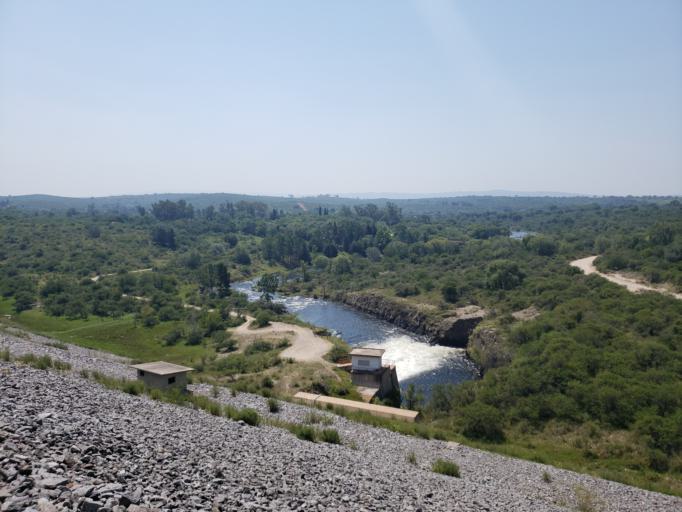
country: AR
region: Cordoba
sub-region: Departamento de Calamuchita
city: Villa Rumipal
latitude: -32.2245
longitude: -64.5672
